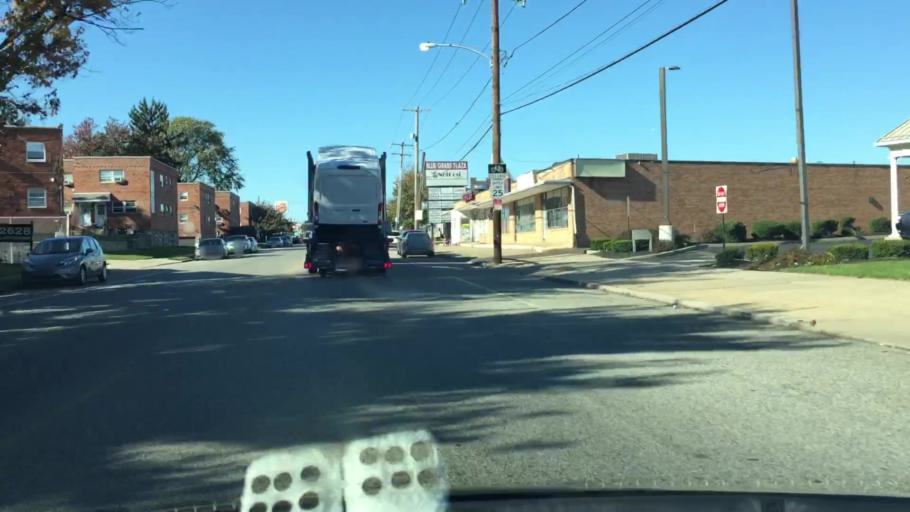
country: US
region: Pennsylvania
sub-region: Montgomery County
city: Rockledge
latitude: 40.0704
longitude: -75.0314
